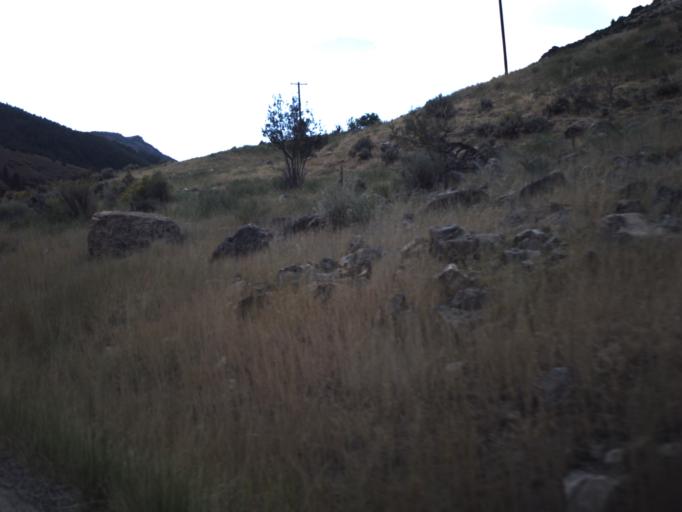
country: US
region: Utah
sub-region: Cache County
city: Millville
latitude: 41.6080
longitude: -111.6132
